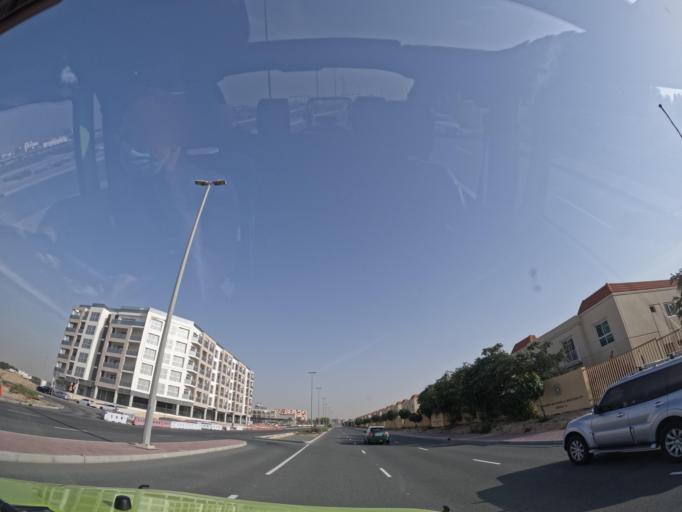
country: AE
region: Dubai
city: Dubai
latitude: 25.1279
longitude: 55.3548
